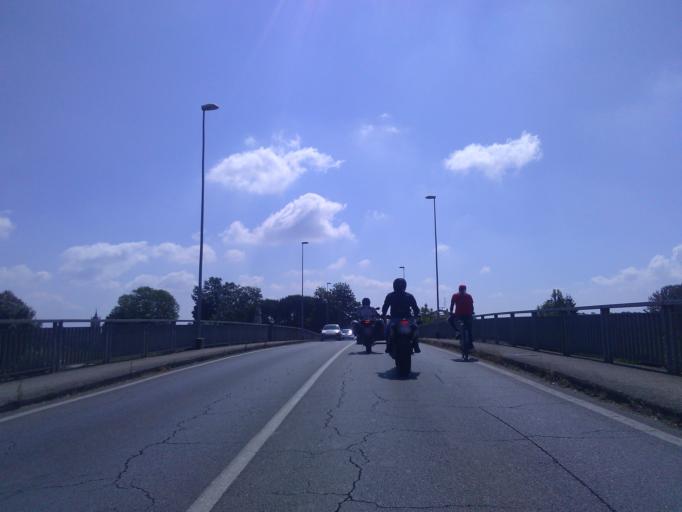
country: IT
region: Tuscany
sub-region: Provincia di Lucca
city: Lucca
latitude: 43.8526
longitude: 10.4487
